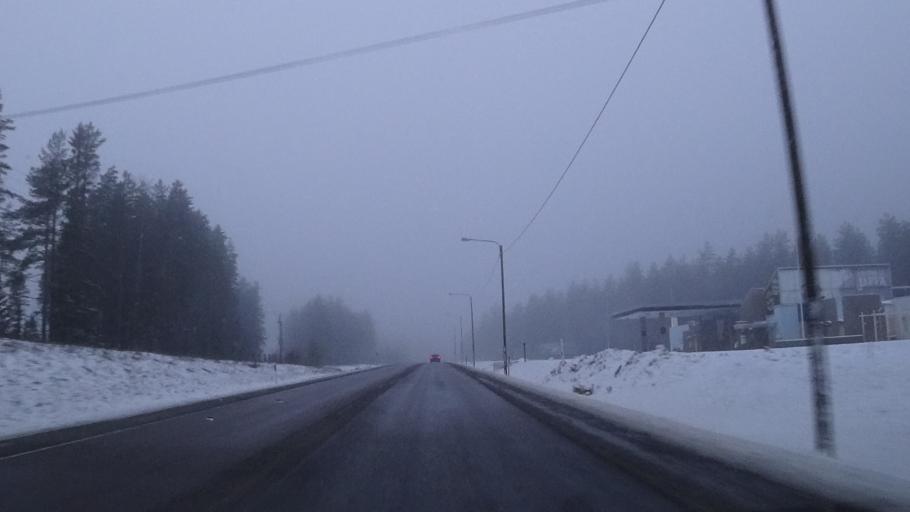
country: FI
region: Paijanne Tavastia
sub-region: Lahti
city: Hollola
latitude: 60.9887
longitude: 25.3924
